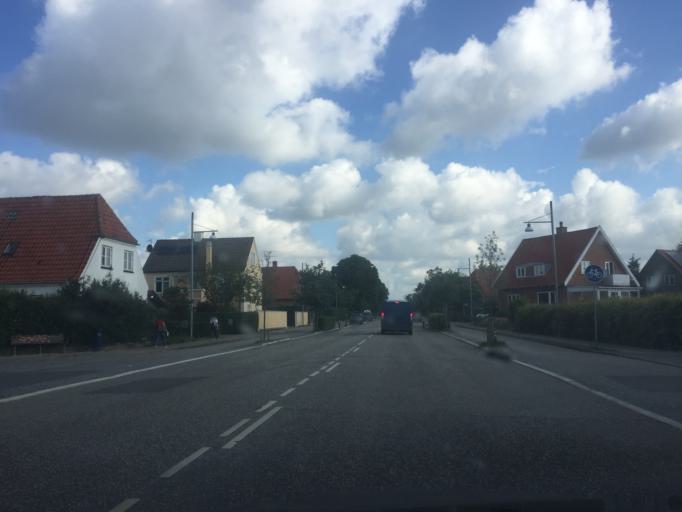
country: DK
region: Capital Region
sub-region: Glostrup Kommune
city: Glostrup
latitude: 55.6684
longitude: 12.4005
